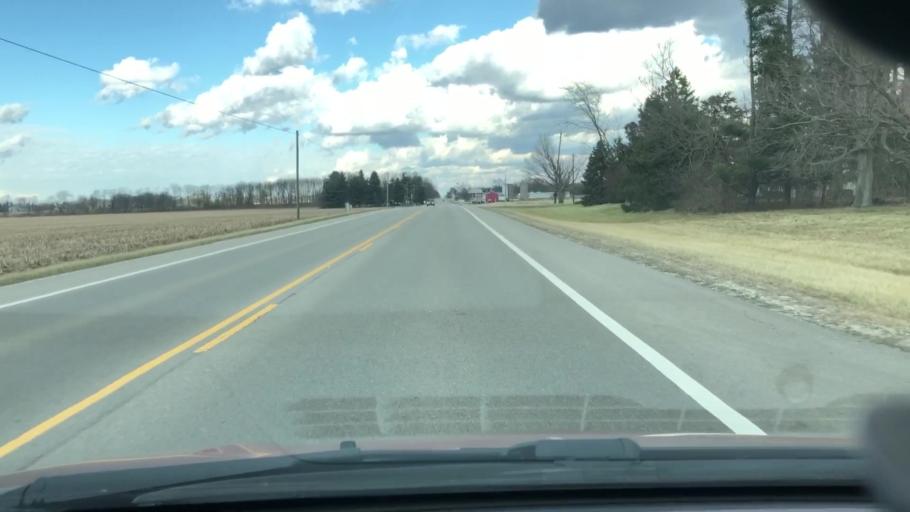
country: US
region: Ohio
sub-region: Greene County
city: Yellow Springs
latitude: 39.8201
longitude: -83.8764
